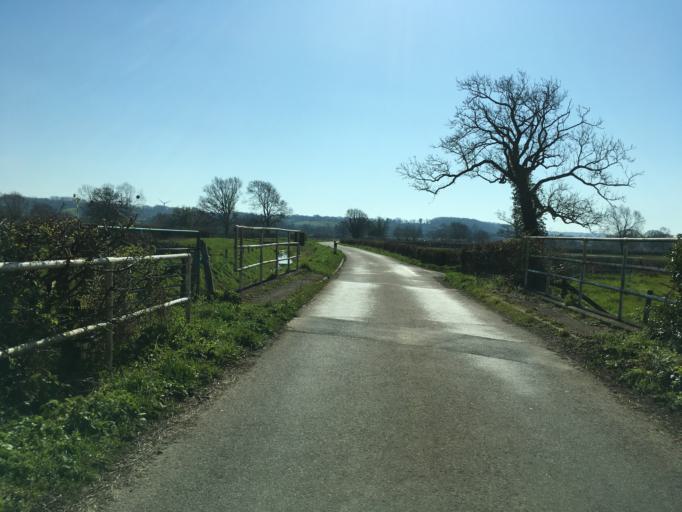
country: GB
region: England
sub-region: South Gloucestershire
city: Hill
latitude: 51.6447
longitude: -2.5105
